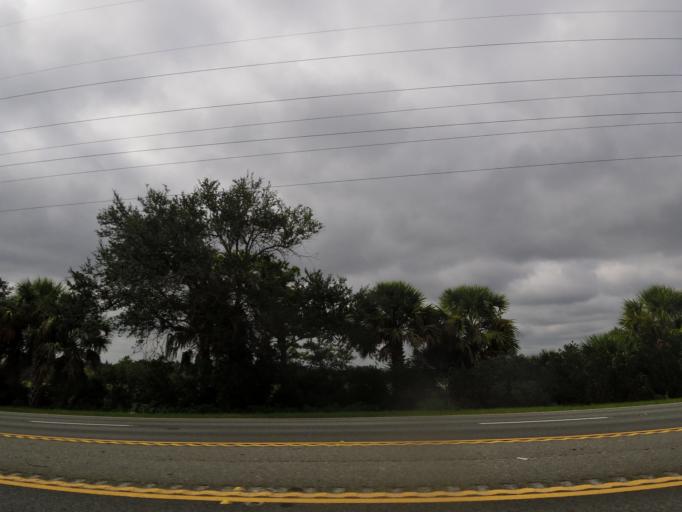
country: US
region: Georgia
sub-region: Glynn County
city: Brunswick
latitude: 31.1615
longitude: -81.4712
